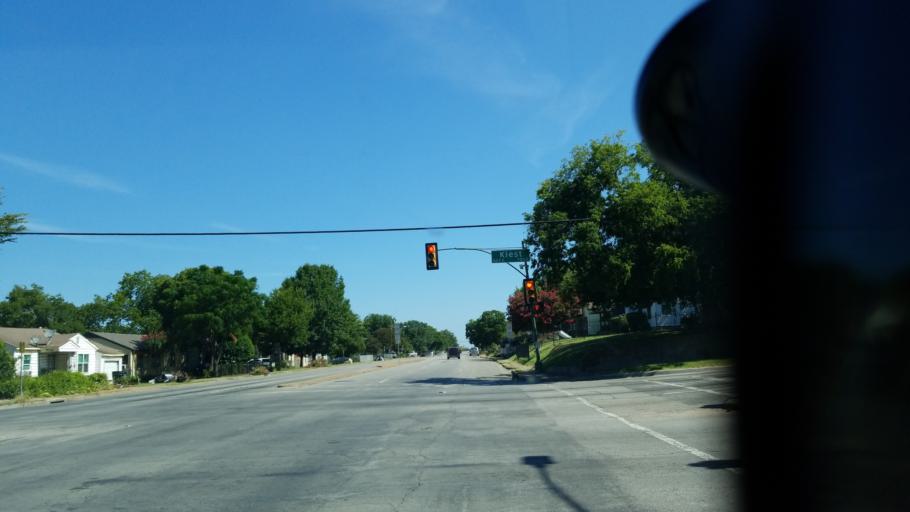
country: US
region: Texas
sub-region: Dallas County
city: Dallas
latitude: 32.7058
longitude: -96.8145
